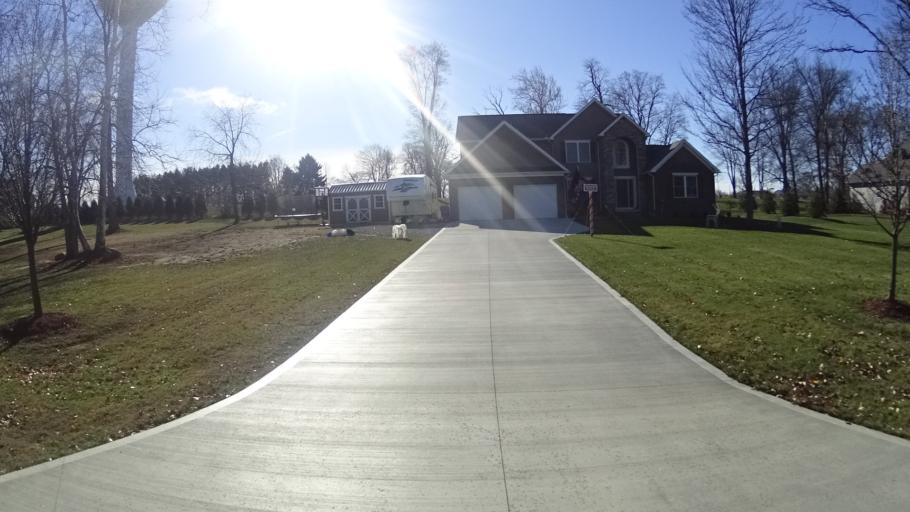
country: US
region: Ohio
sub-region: Lorain County
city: South Amherst
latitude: 41.3760
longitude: -82.2866
